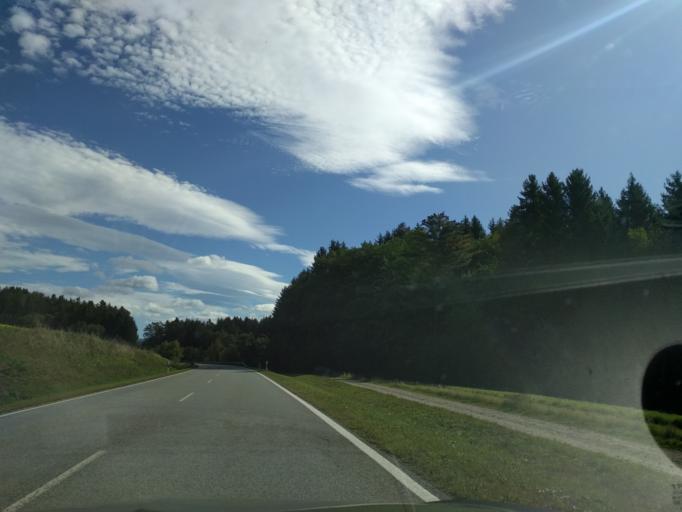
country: DE
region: Bavaria
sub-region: Upper Palatinate
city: Grafenwiesen
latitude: 49.2089
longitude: 12.9052
